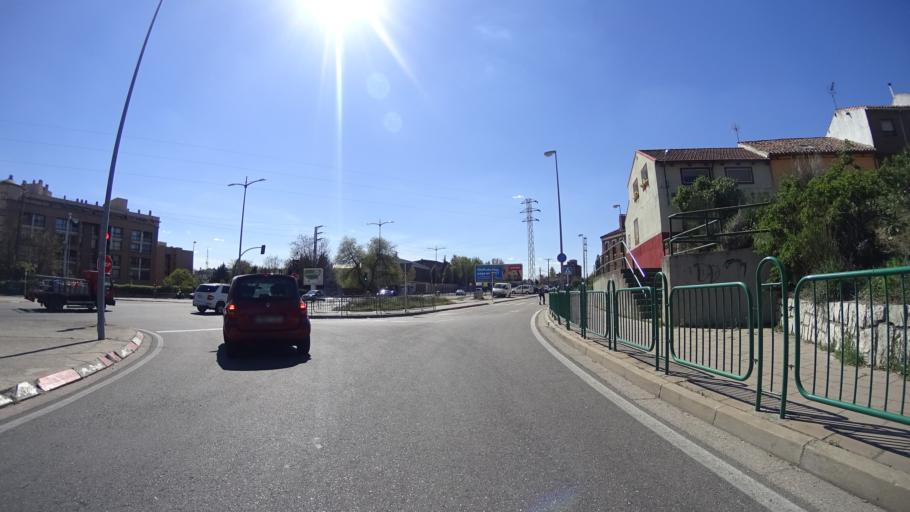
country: ES
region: Castille and Leon
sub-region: Provincia de Valladolid
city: Valladolid
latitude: 41.6612
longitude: -4.7425
